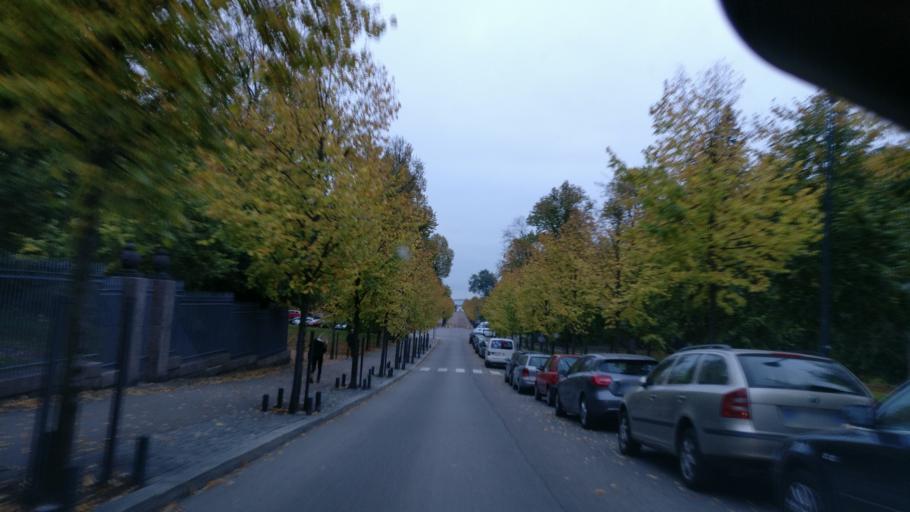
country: FI
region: Uusimaa
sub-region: Helsinki
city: Helsinki
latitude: 60.1589
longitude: 24.9552
